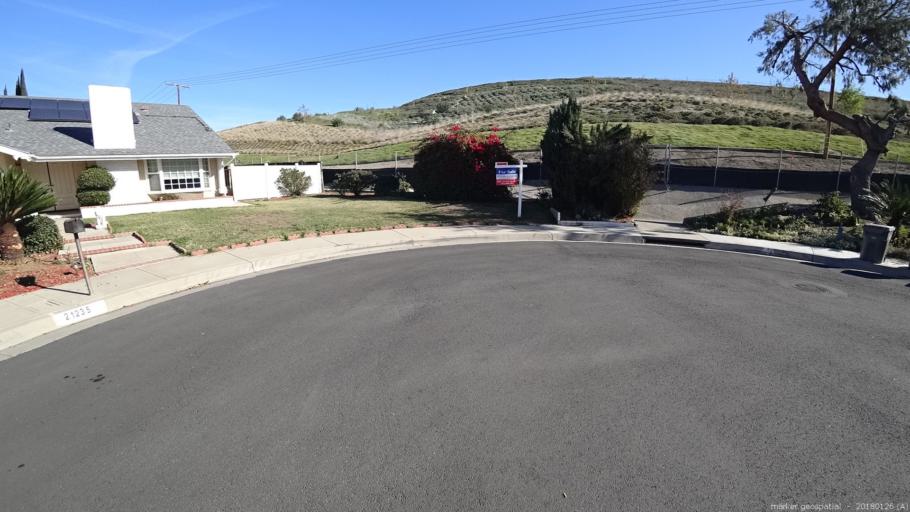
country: US
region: California
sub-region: Los Angeles County
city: Walnut
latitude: 34.0039
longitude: -117.8415
